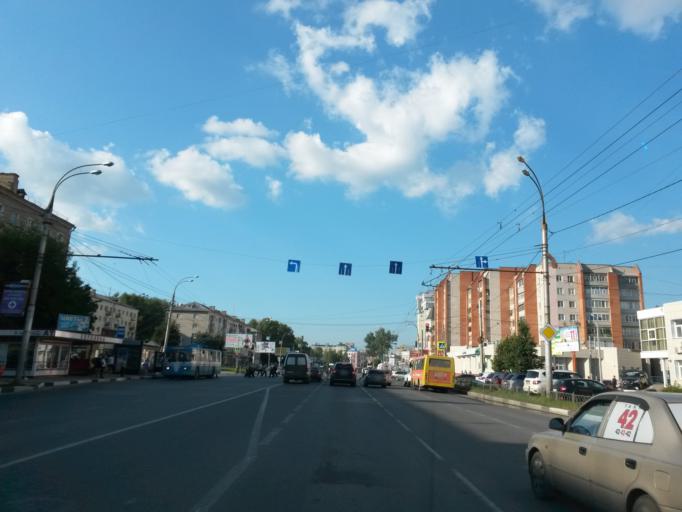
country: RU
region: Ivanovo
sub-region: Gorod Ivanovo
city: Ivanovo
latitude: 56.9709
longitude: 40.9737
